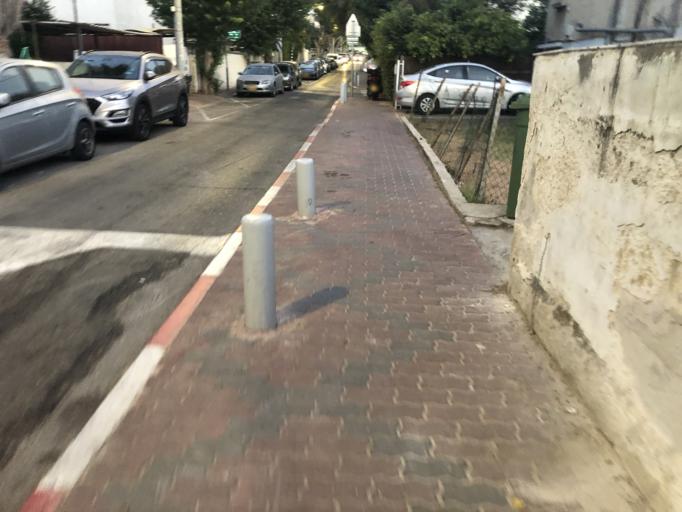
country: IL
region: Tel Aviv
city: Giv`atayim
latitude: 32.0699
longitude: 34.8200
